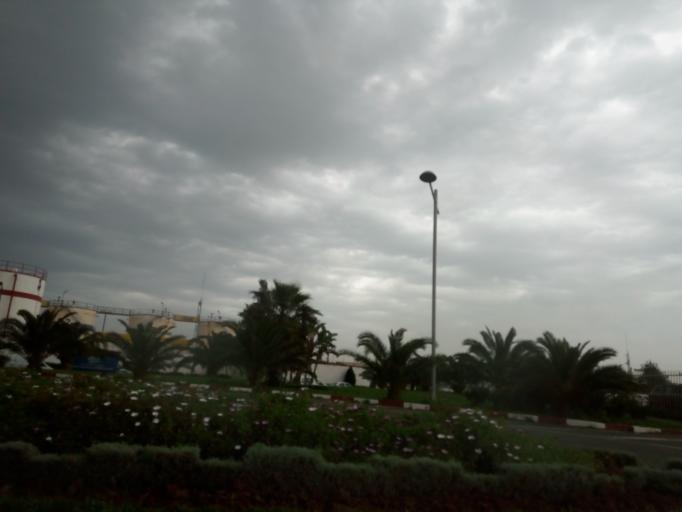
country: DZ
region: Alger
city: Dar el Beida
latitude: 36.7028
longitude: 3.2098
